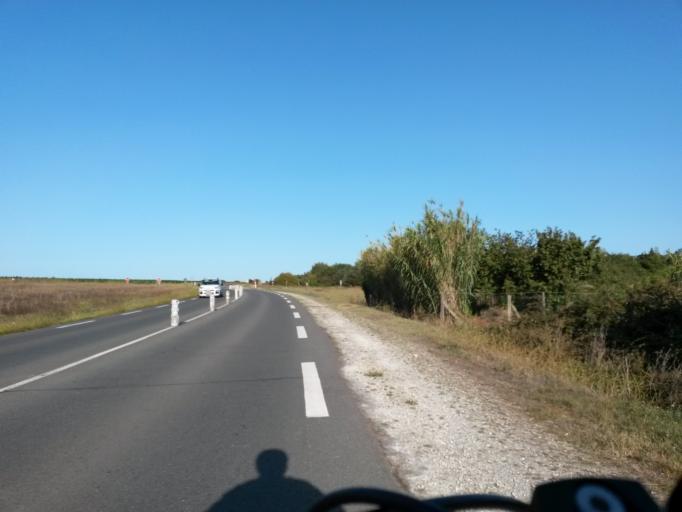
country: FR
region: Poitou-Charentes
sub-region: Departement de la Charente-Maritime
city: Rivedoux-Plage
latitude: 46.1526
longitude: -1.2809
